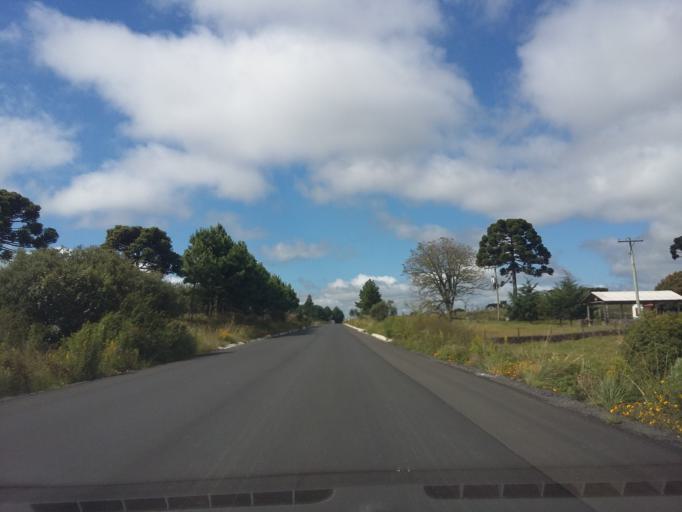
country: BR
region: Santa Catarina
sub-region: Sao Joaquim
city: Sao Joaquim
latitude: -28.0378
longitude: -50.0742
